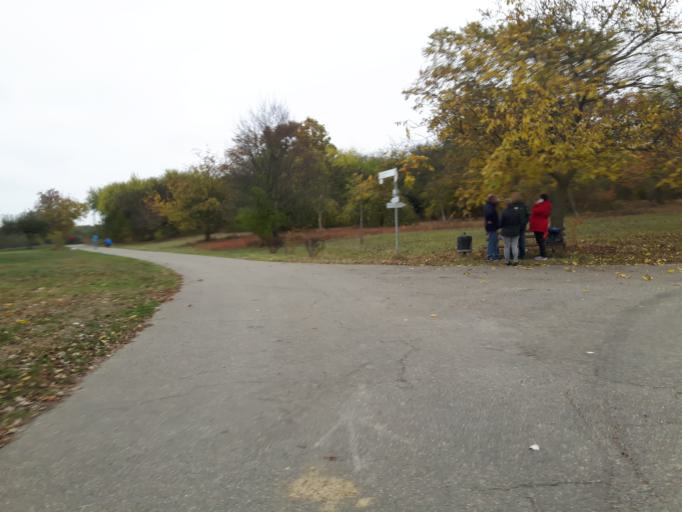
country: DE
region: Baden-Wuerttemberg
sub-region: Karlsruhe Region
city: Malsch
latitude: 49.2284
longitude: 8.6645
